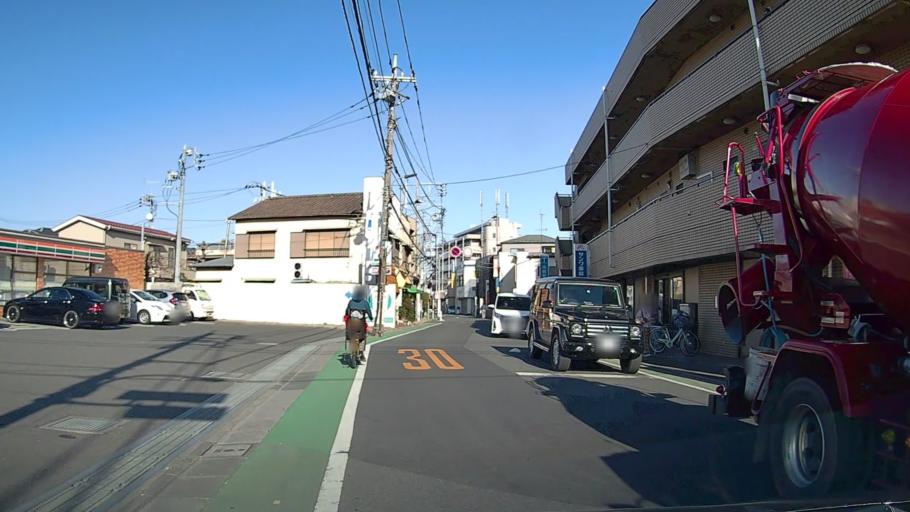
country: JP
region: Tokyo
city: Nishi-Tokyo-shi
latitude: 35.7606
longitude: 139.5753
